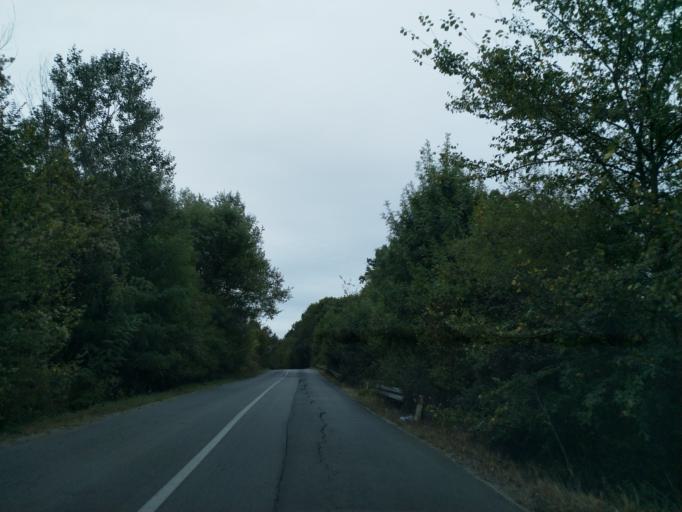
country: RS
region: Central Serbia
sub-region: Pomoravski Okrug
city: Jagodina
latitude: 44.0301
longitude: 21.1951
